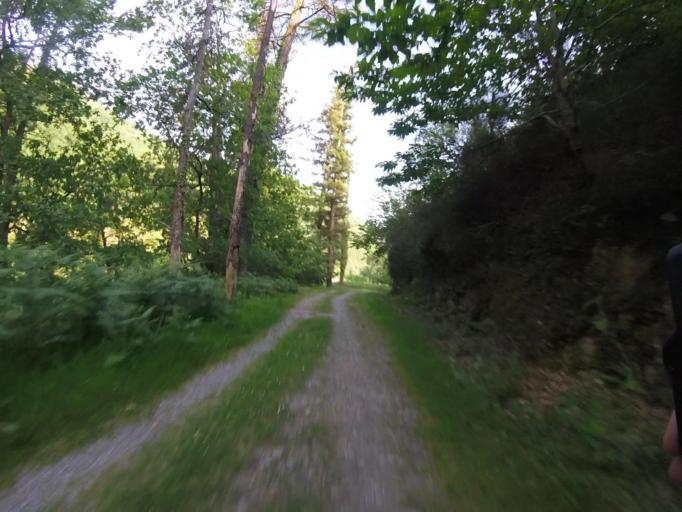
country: ES
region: Navarre
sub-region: Provincia de Navarra
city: Arano
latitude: 43.2325
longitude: -1.8698
